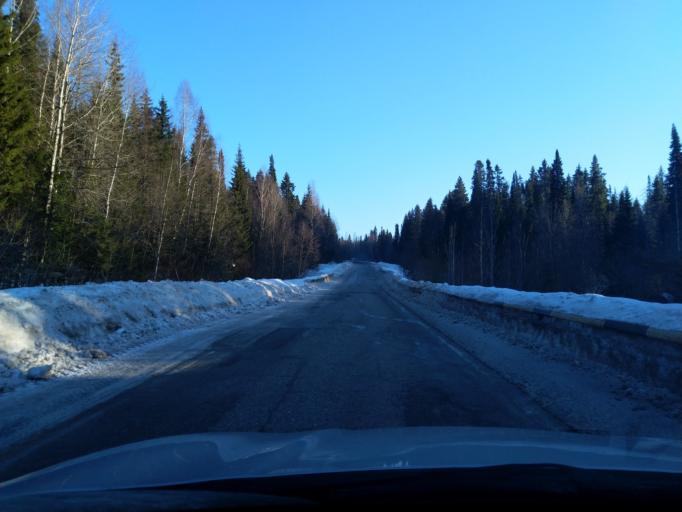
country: RU
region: Perm
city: Polazna
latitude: 58.3008
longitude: 56.4745
